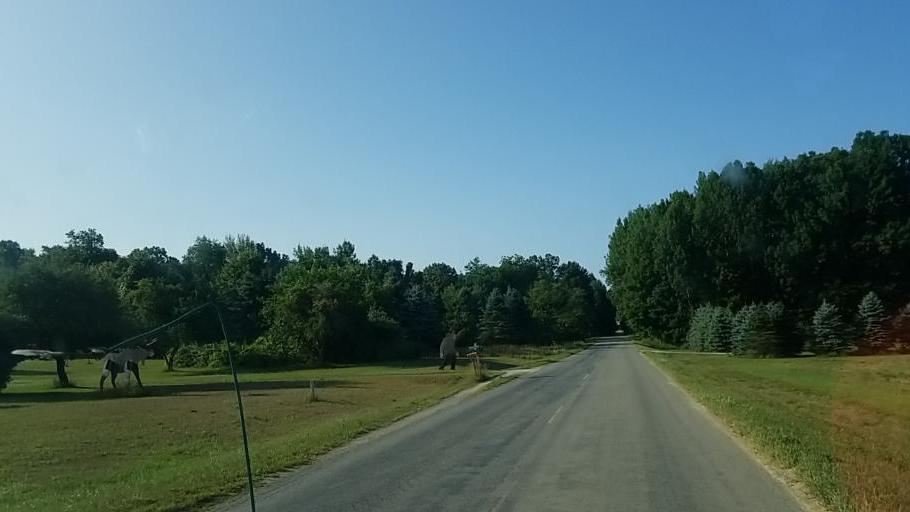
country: US
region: Michigan
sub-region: Newaygo County
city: Newaygo
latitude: 43.3776
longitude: -85.8307
